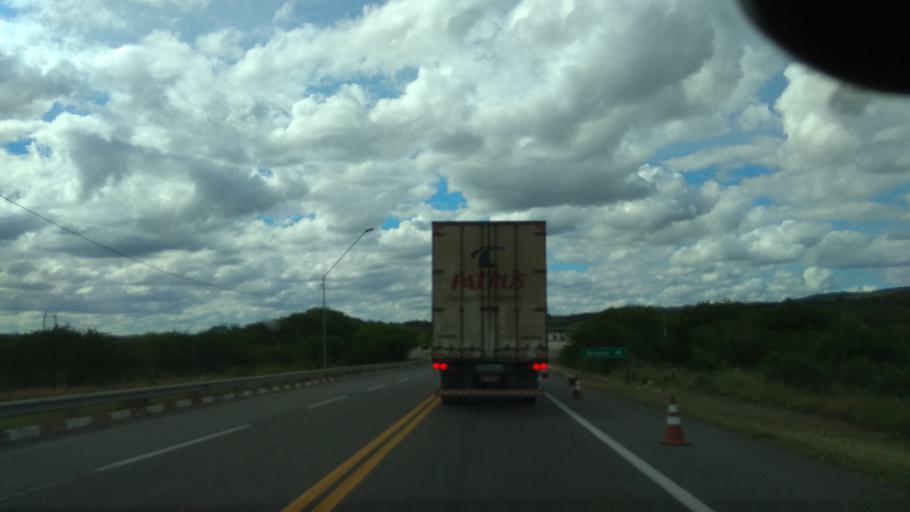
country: BR
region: Bahia
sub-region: Santa Ines
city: Santa Ines
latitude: -12.9857
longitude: -39.9438
